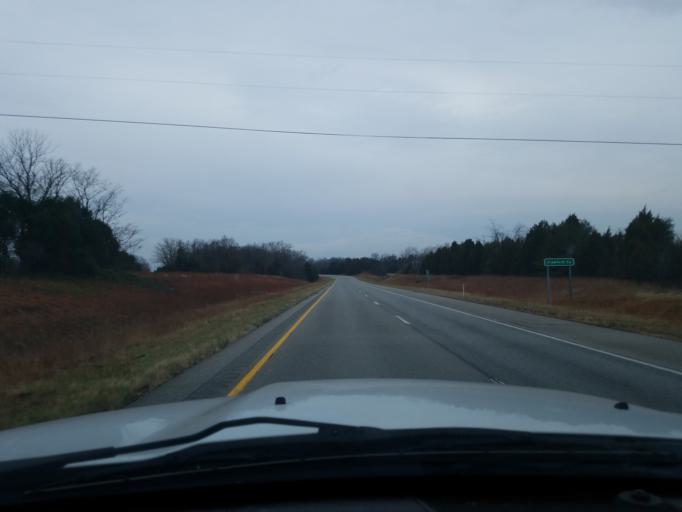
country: US
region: Indiana
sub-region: Harrison County
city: Corydon
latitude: 38.2517
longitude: -86.2754
